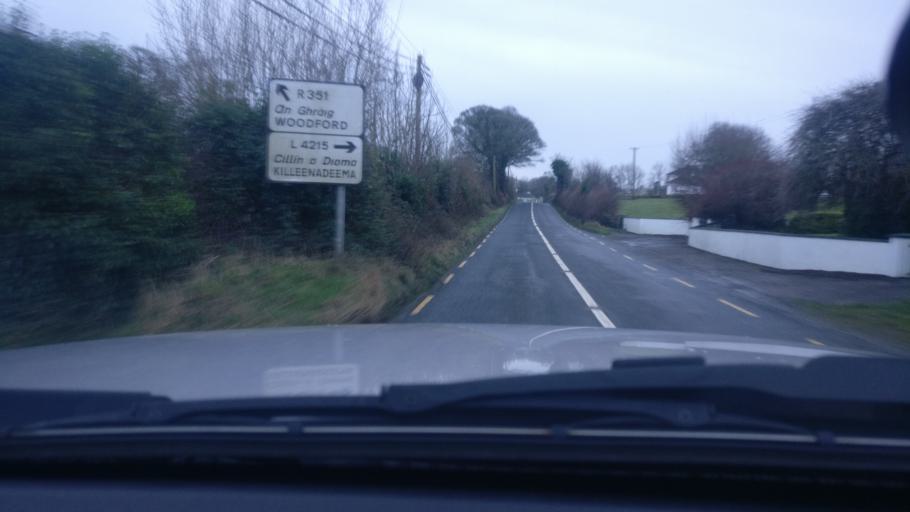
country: IE
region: Connaught
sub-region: County Galway
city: Loughrea
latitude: 53.1639
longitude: -8.5204
